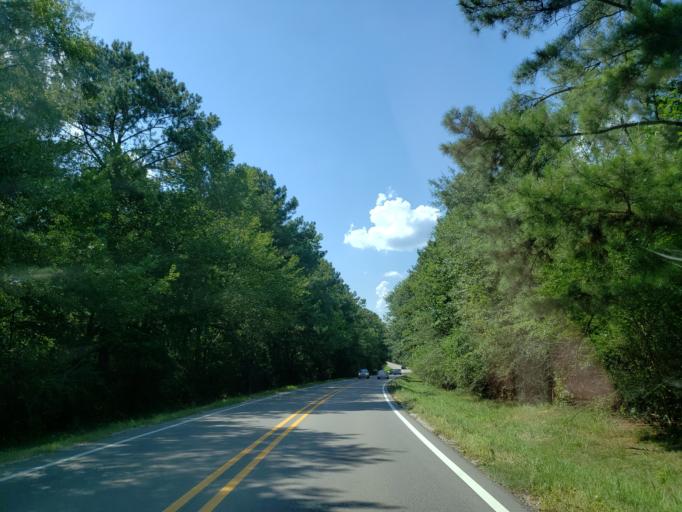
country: US
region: Mississippi
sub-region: Lamar County
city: Sumrall
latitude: 31.3820
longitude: -89.5258
